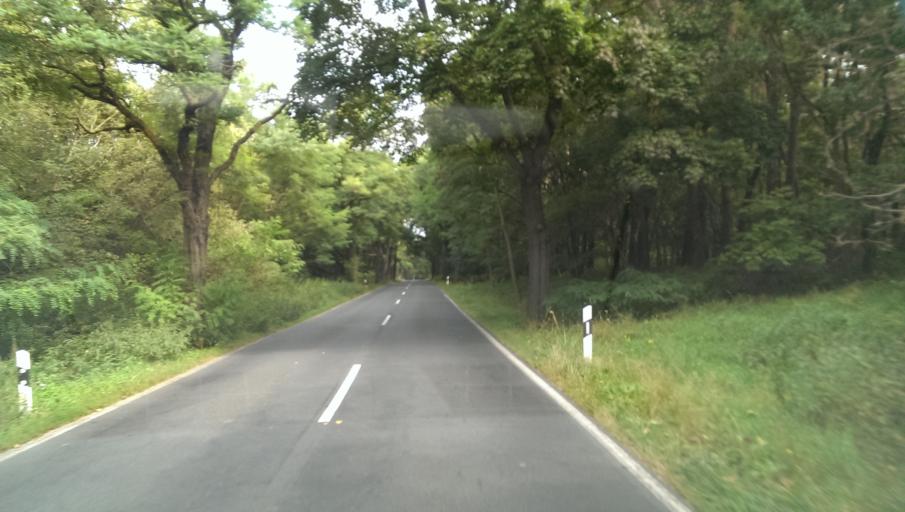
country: DE
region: Brandenburg
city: Trebbin
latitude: 52.1981
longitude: 13.2475
